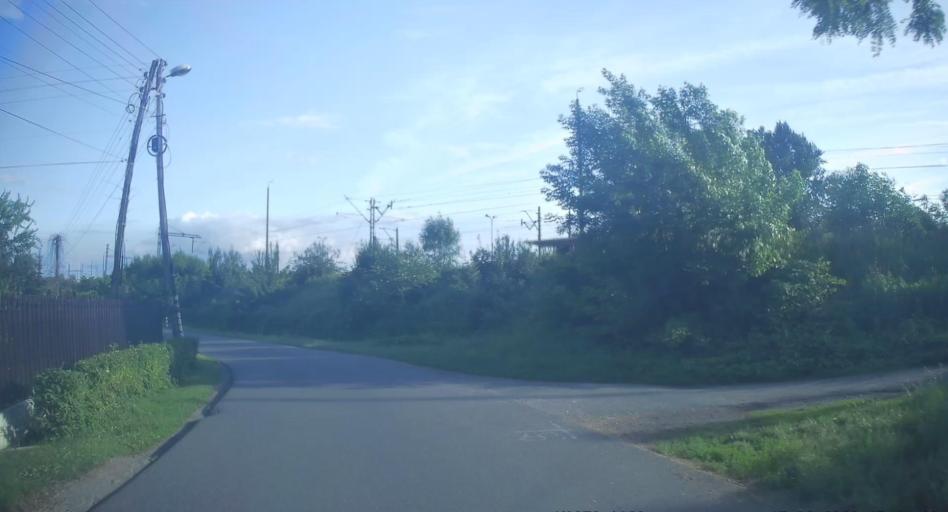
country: PL
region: Lesser Poland Voivodeship
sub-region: Powiat oswiecimski
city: Babice
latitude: 50.0728
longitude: 19.1863
